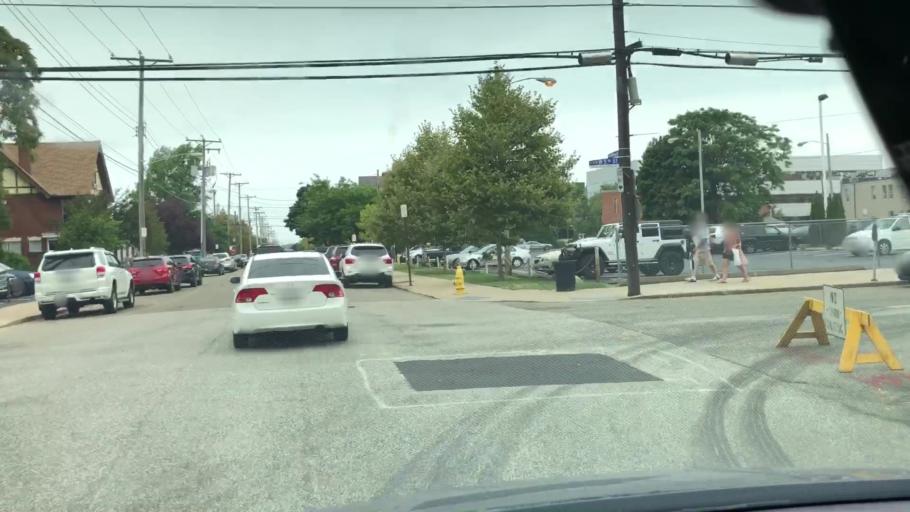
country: US
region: Pennsylvania
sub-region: Erie County
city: Erie
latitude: 42.1299
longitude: -80.0872
